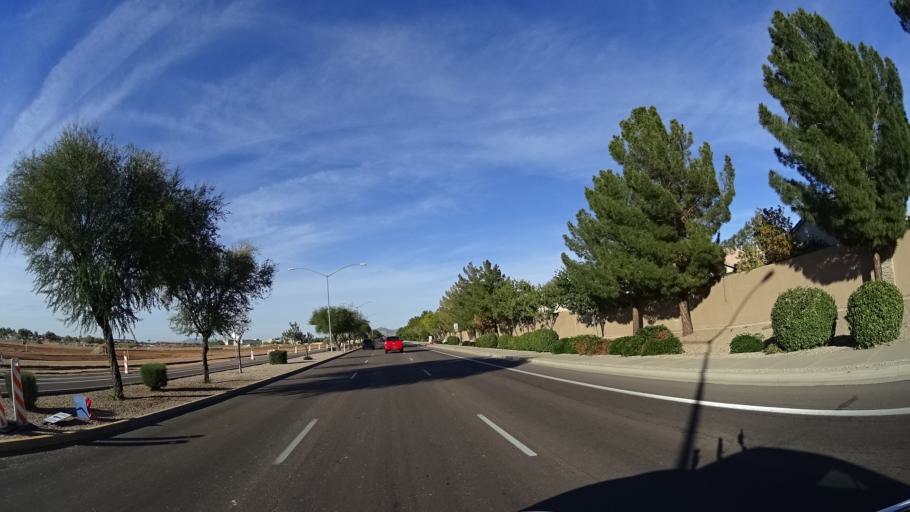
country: US
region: Arizona
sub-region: Pinal County
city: Apache Junction
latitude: 33.3723
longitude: -111.6365
